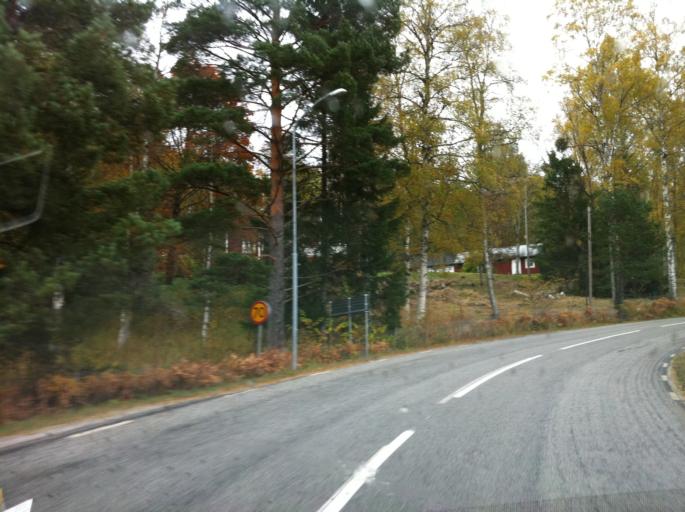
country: SE
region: OErebro
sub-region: Lindesbergs Kommun
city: Stora
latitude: 59.6590
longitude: 15.0774
